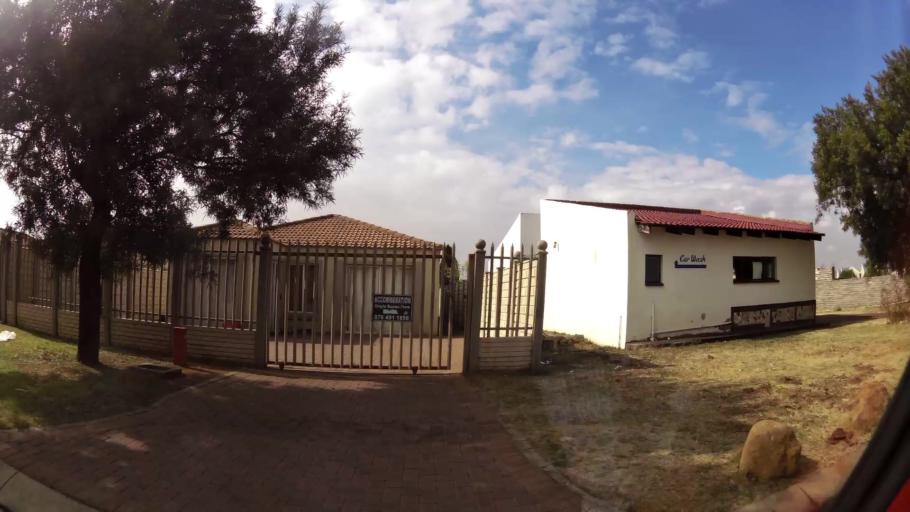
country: ZA
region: Gauteng
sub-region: Sedibeng District Municipality
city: Vanderbijlpark
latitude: -26.7164
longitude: 27.8845
